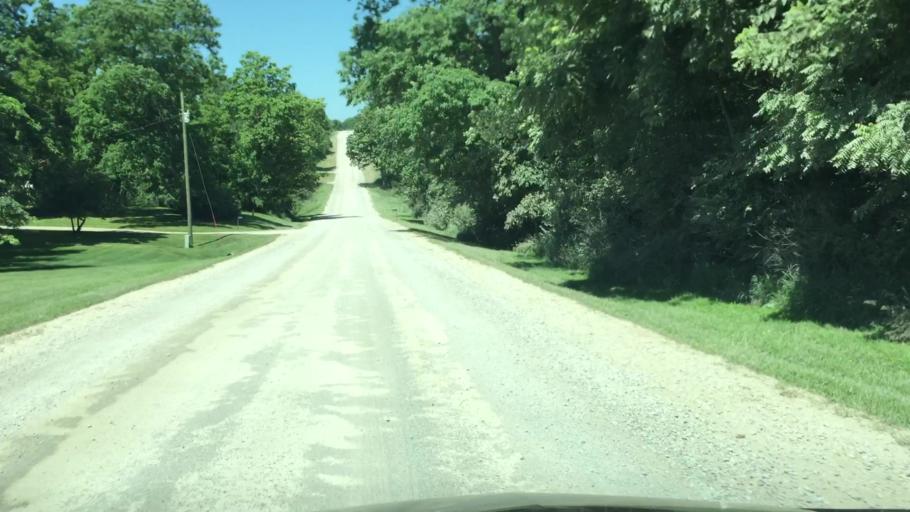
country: US
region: Iowa
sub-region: Linn County
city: Ely
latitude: 41.8328
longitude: -91.5729
